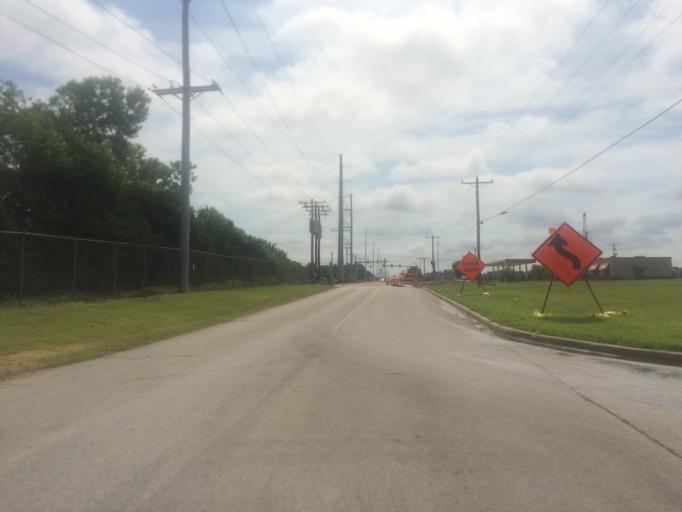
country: US
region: Oklahoma
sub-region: Cleveland County
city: Noble
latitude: 35.1751
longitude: -97.4260
